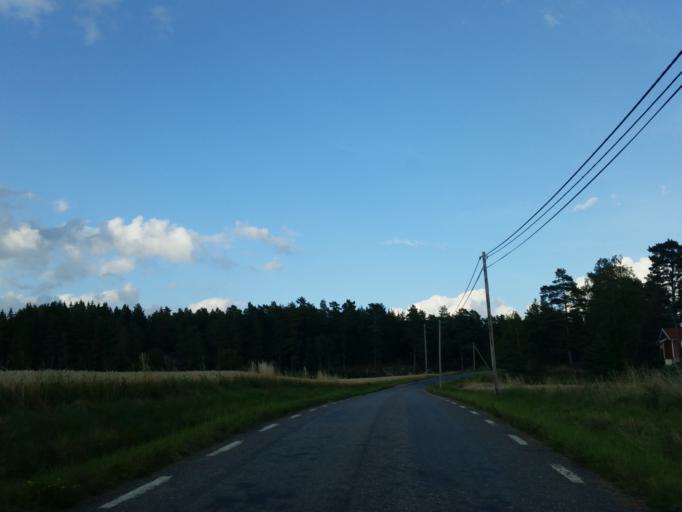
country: SE
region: Stockholm
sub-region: Nykvarns Kommun
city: Nykvarn
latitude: 59.2526
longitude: 17.4130
